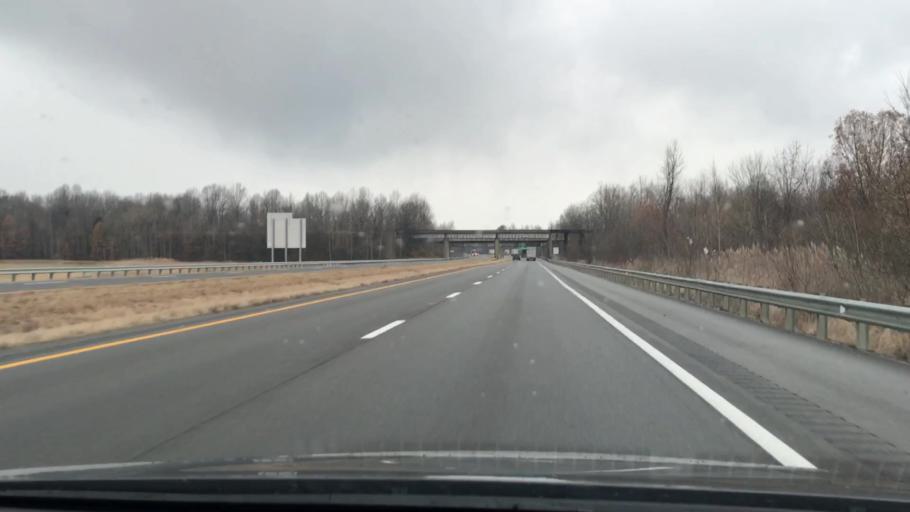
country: US
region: Kentucky
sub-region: Hopkins County
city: Madisonville
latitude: 37.3053
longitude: -87.4662
